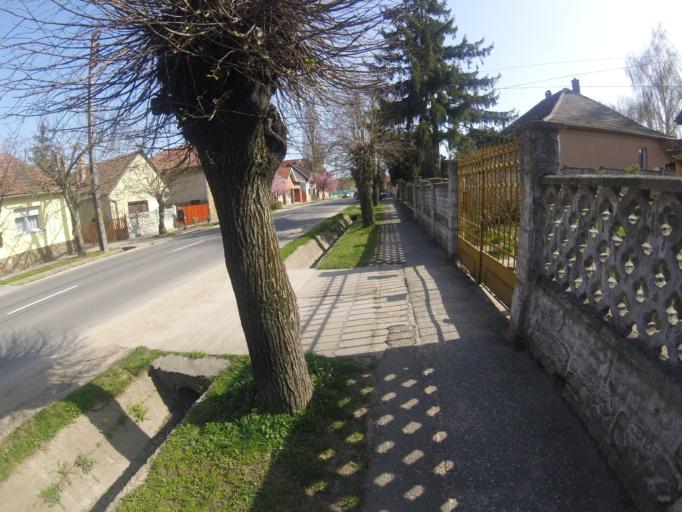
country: HU
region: Pest
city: Pilisvorosvar
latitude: 47.6216
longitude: 18.9019
